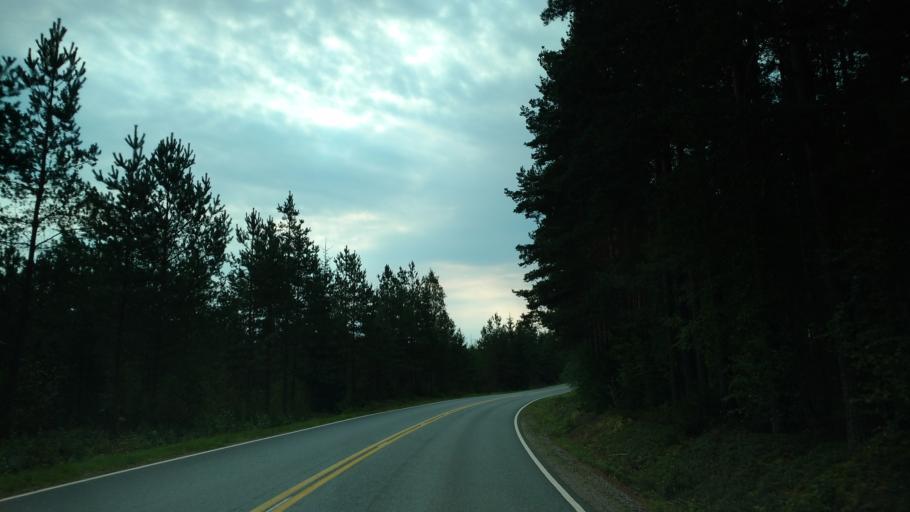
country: FI
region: Varsinais-Suomi
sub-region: Loimaa
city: Koski Tl
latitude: 60.6262
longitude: 23.1109
